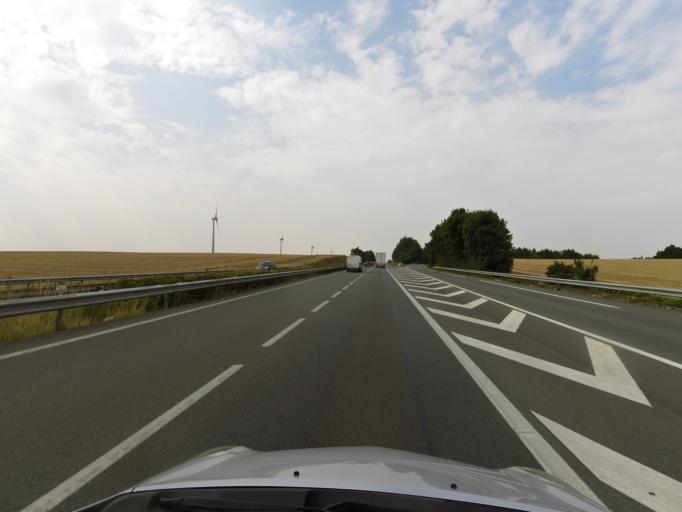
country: FR
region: Picardie
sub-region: Departement de l'Aisne
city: Holnon
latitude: 49.9184
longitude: 3.2330
